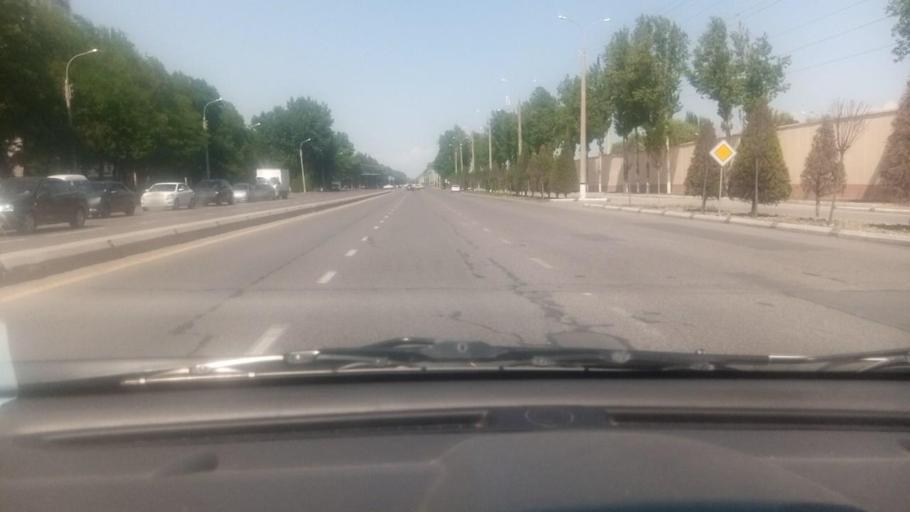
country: UZ
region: Toshkent
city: Salor
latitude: 41.3212
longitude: 69.3623
